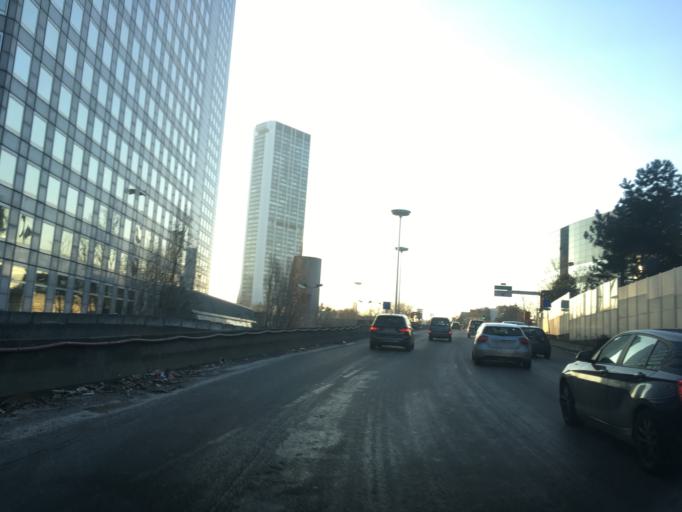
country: FR
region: Ile-de-France
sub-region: Departement des Hauts-de-Seine
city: La Defense
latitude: 48.8906
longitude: 2.2344
